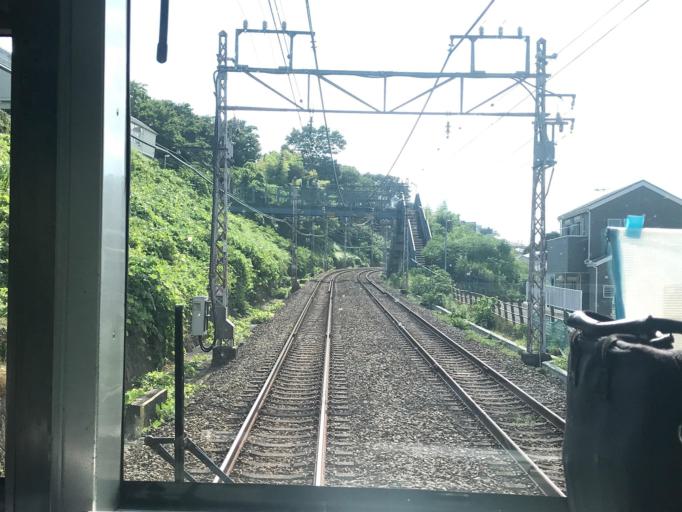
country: JP
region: Kanagawa
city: Hadano
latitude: 35.3647
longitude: 139.2372
